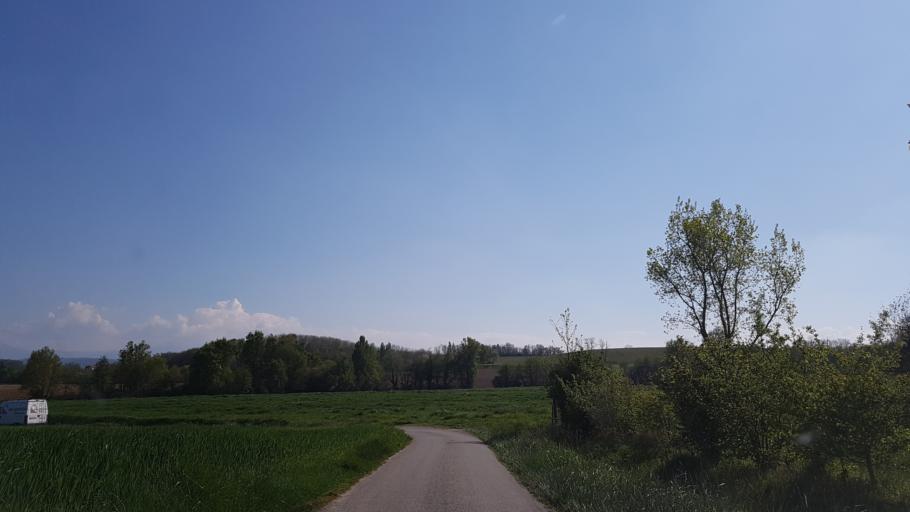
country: FR
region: Midi-Pyrenees
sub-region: Departement de l'Ariege
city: La Tour-du-Crieu
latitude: 43.0983
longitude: 1.7165
